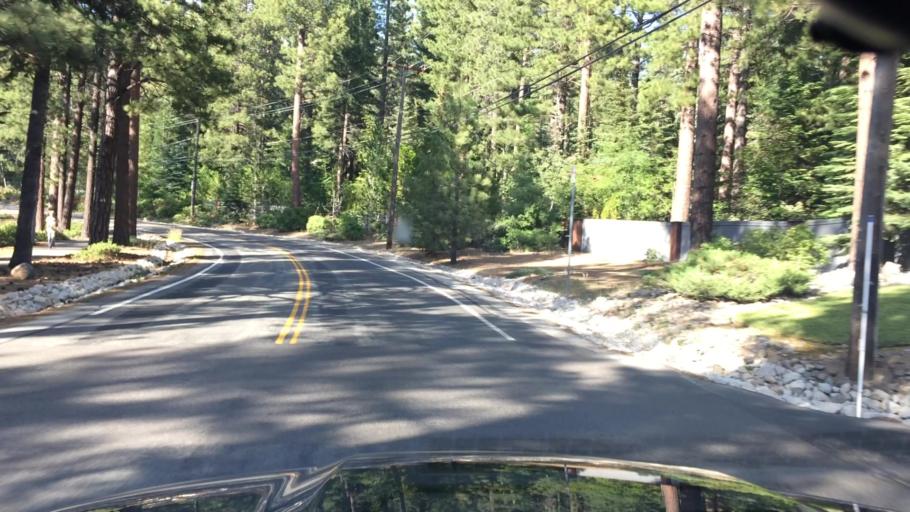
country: US
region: Nevada
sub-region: Washoe County
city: Incline Village
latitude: 39.2424
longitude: -119.9382
